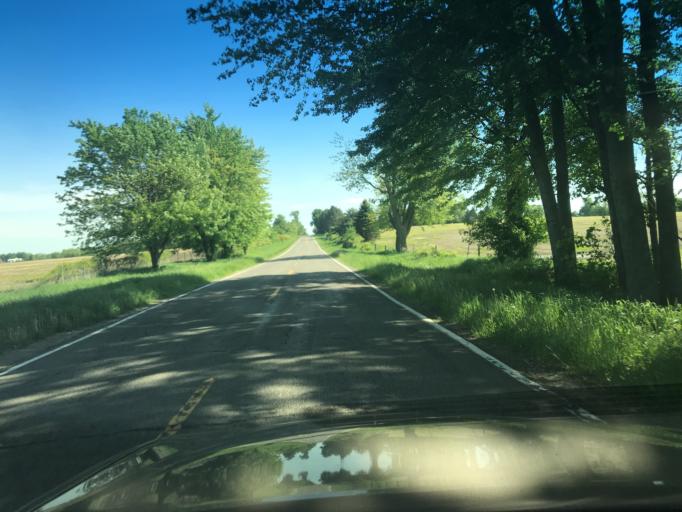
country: US
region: Michigan
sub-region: Ingham County
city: Mason
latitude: 42.5432
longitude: -84.4626
